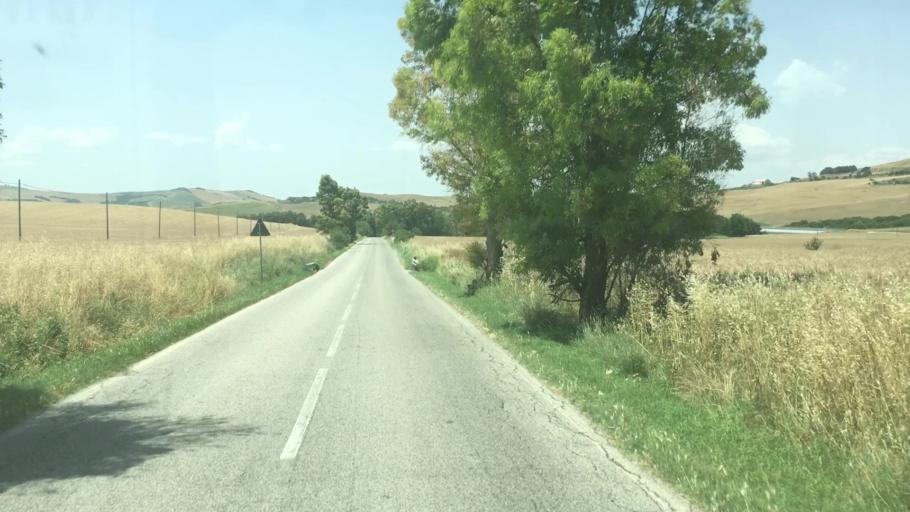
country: IT
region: Basilicate
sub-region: Provincia di Matera
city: La Martella
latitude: 40.6687
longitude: 16.4855
